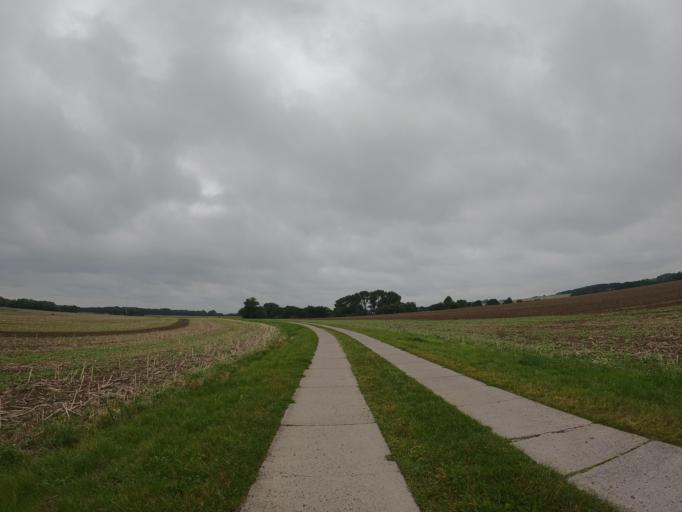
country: DE
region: Mecklenburg-Vorpommern
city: Poseritz
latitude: 54.2773
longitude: 13.2461
